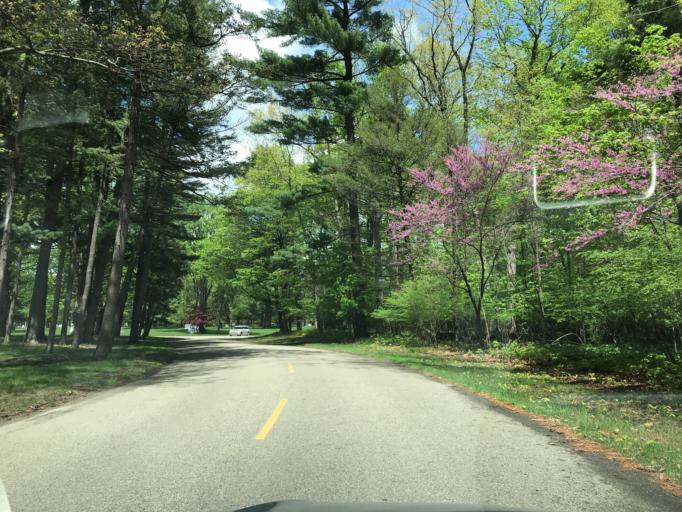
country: US
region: Michigan
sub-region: Oakland County
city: Franklin
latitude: 42.4779
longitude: -83.3006
